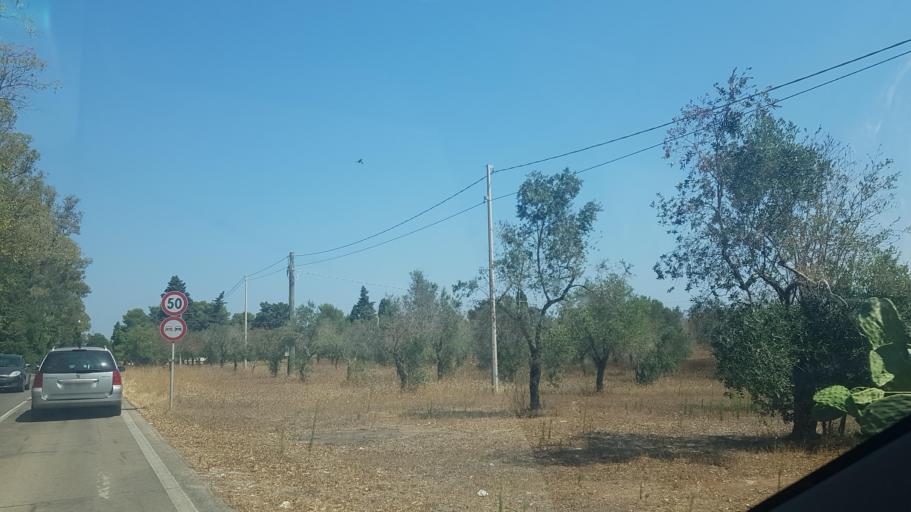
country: IT
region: Apulia
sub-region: Provincia di Lecce
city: Otranto
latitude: 40.1967
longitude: 18.4356
